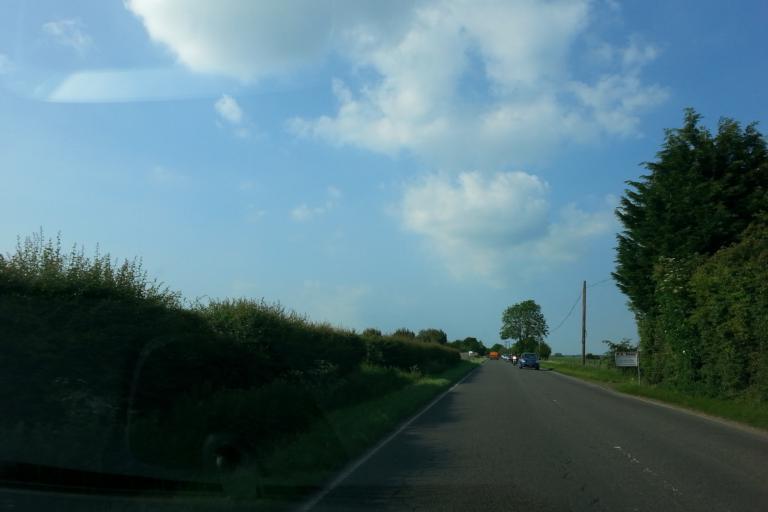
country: GB
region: England
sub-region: Cambridgeshire
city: Earith
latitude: 52.3309
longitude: 0.0649
